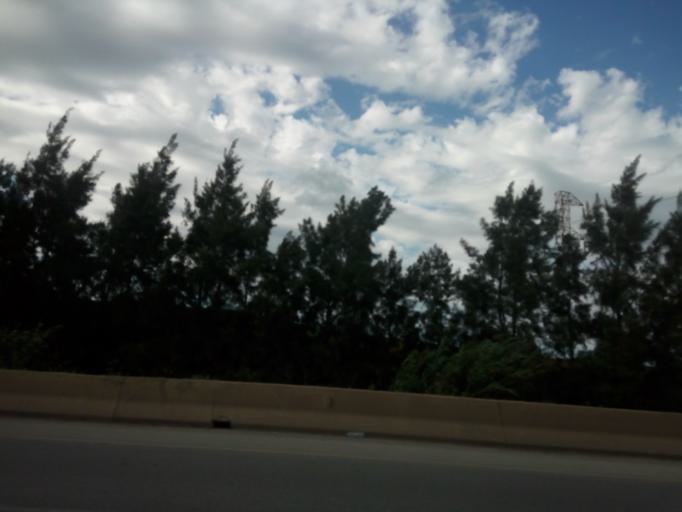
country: DZ
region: Tipaza
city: El Affroun
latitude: 36.4489
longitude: 2.6555
